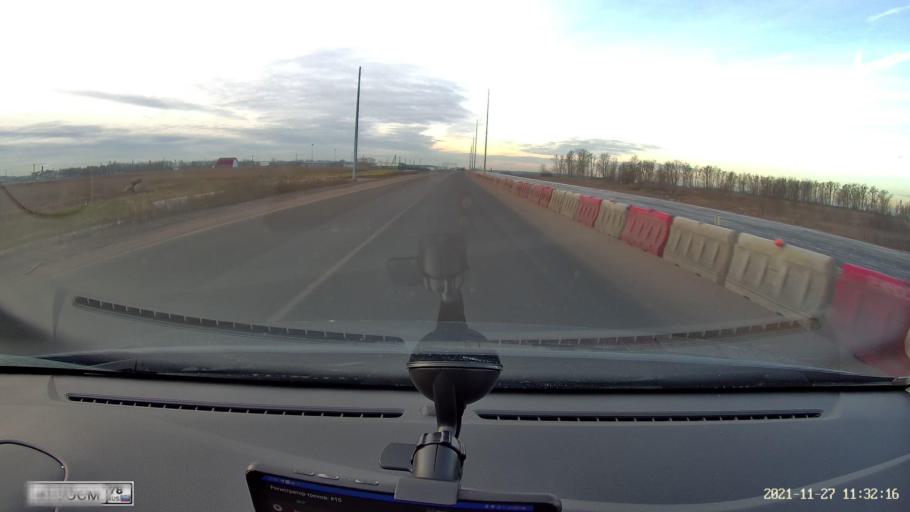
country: RU
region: St.-Petersburg
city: Krasnoye Selo
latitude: 59.7151
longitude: 30.0388
